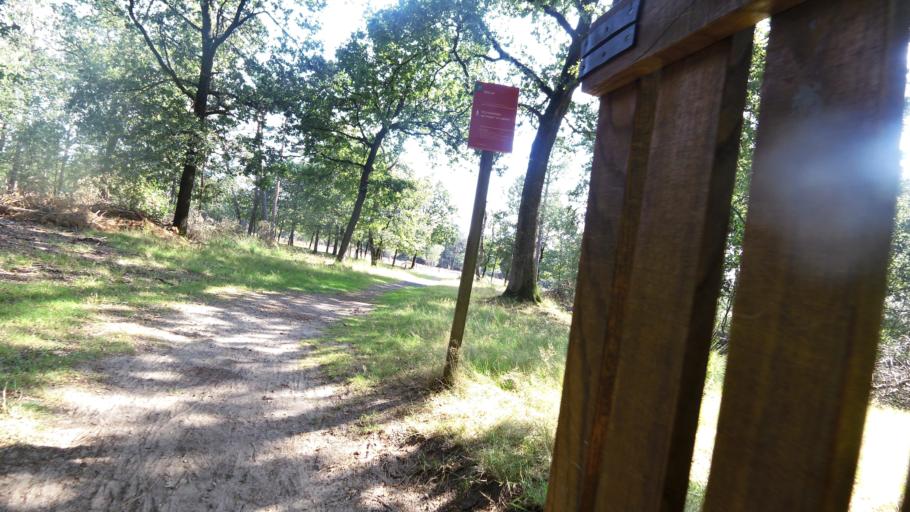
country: NL
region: Gelderland
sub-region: Gemeente Ede
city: Harskamp
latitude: 52.1500
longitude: 5.7474
